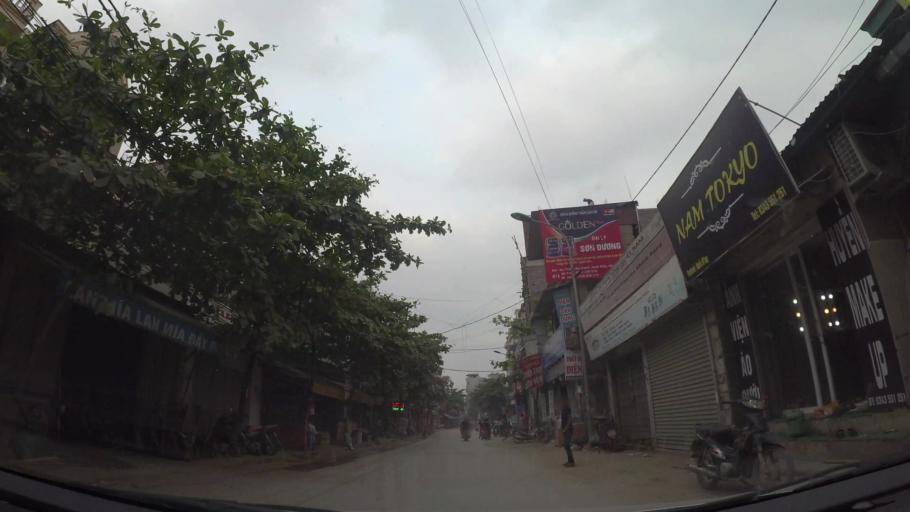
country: VN
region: Ha Noi
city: Cau Dien
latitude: 21.0348
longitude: 105.7361
